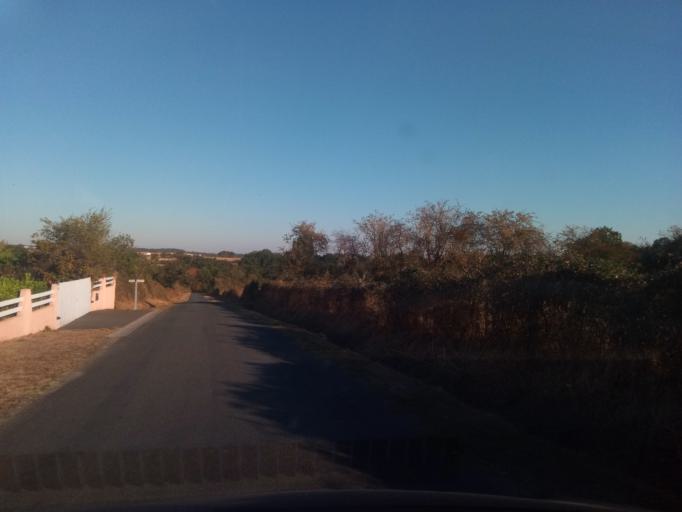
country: FR
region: Poitou-Charentes
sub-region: Departement de la Vienne
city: Montmorillon
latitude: 46.4090
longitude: 0.8696
